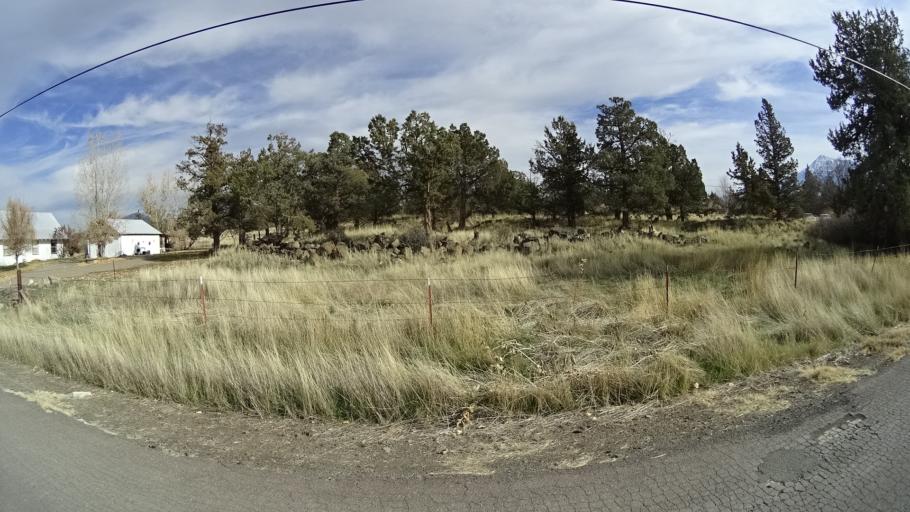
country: US
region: California
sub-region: Siskiyou County
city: Weed
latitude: 41.5975
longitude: -122.4033
